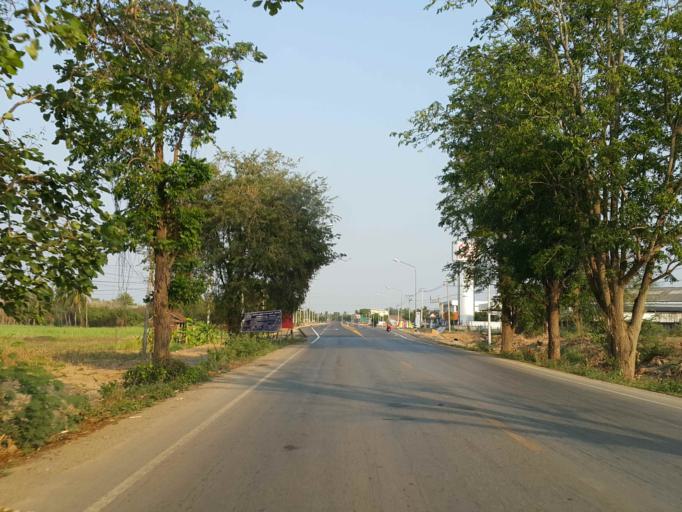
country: TH
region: Sukhothai
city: Sawankhalok
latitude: 17.3076
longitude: 99.8175
